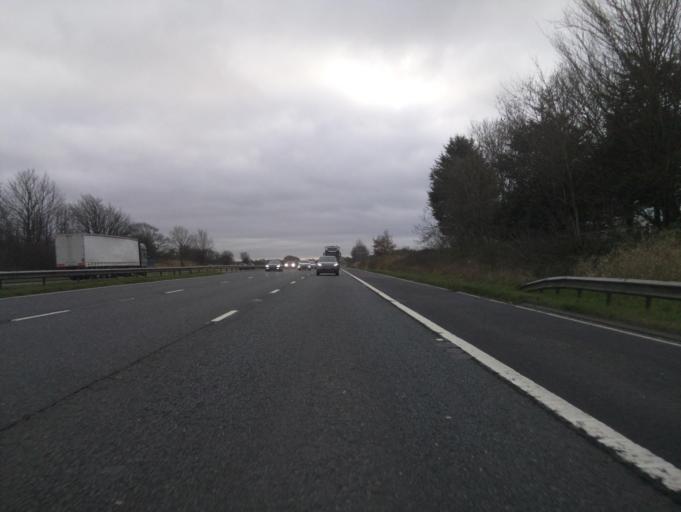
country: GB
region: England
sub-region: Lancashire
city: Goosnargh
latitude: 53.8283
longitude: -2.7188
